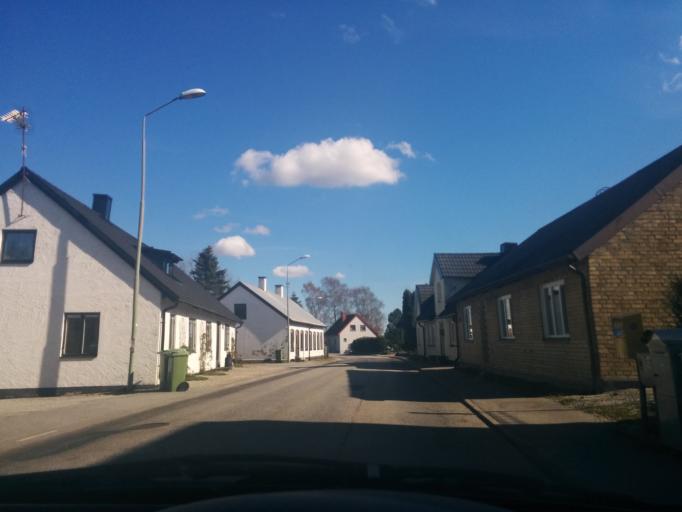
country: SE
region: Skane
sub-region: Lunds Kommun
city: Genarp
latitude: 55.6218
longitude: 13.3163
